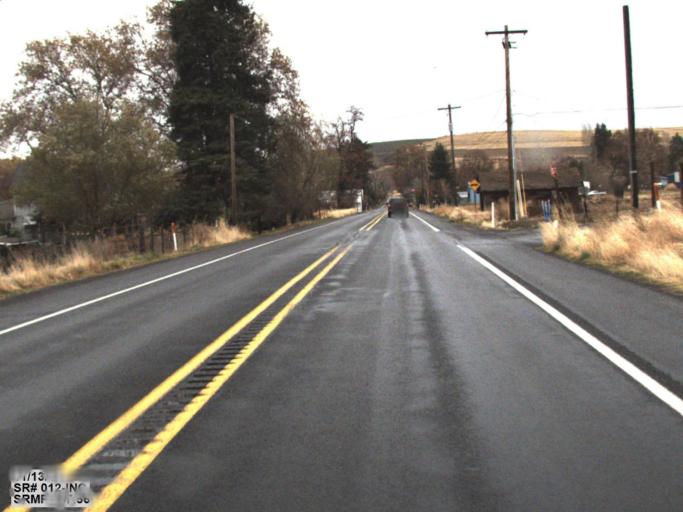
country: US
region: Washington
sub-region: Walla Walla County
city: Waitsburg
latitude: 46.1383
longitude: -118.1602
